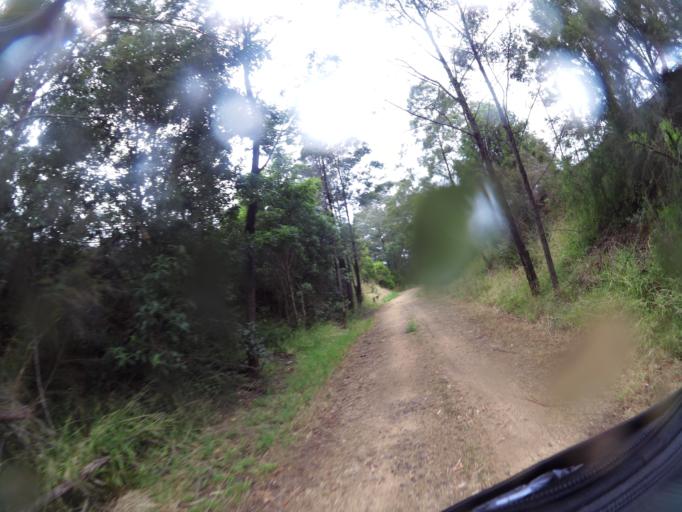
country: AU
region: Victoria
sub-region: East Gippsland
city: Lakes Entrance
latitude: -37.7630
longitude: 147.8208
